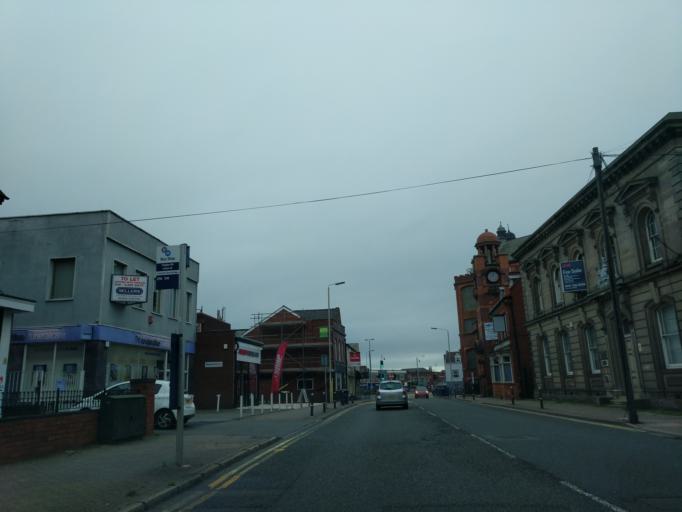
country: GB
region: England
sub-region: Dudley
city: Stourbridge
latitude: 52.4538
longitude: -2.1434
